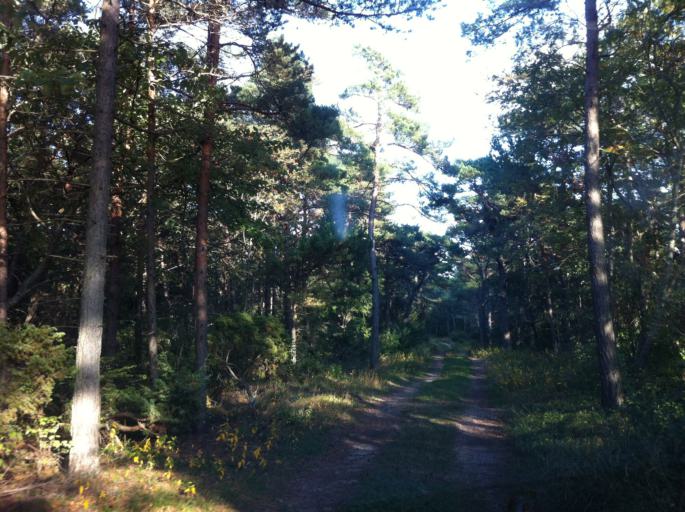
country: SE
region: Gotland
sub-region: Gotland
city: Slite
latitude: 57.4209
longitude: 18.9213
